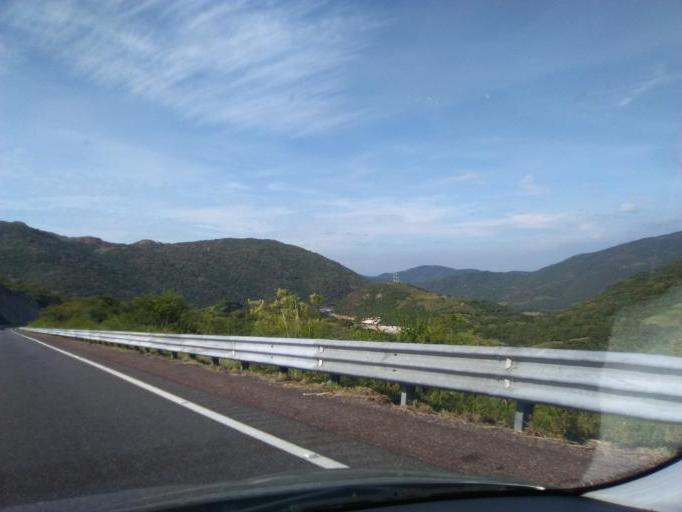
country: MX
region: Guerrero
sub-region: Huitzuco de los Figueroa
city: Ciudad de Huitzuco
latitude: 18.3096
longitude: -99.2016
